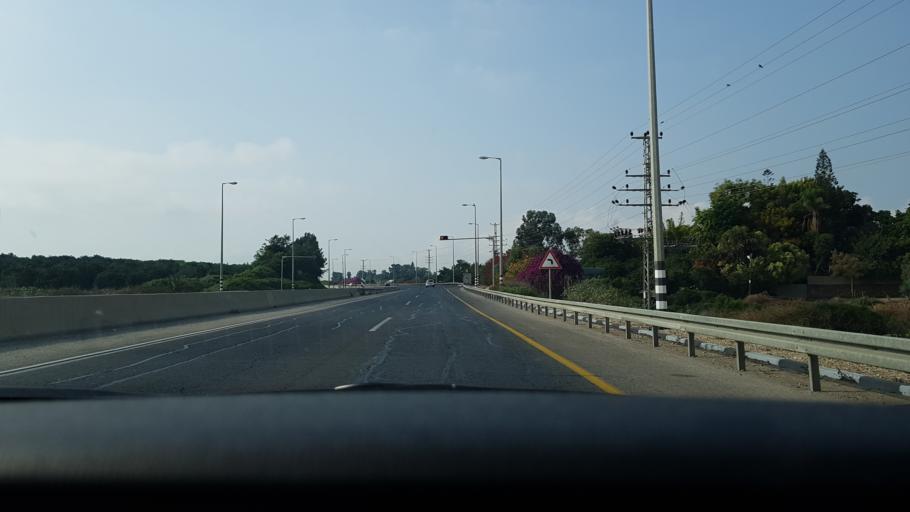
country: IL
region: Central District
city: Ness Ziona
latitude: 31.9447
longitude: 34.7814
